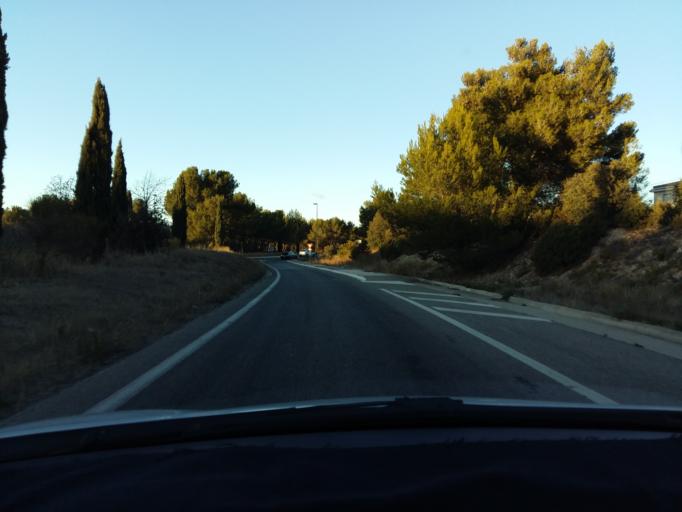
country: FR
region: Provence-Alpes-Cote d'Azur
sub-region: Departement des Bouches-du-Rhone
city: Cabries
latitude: 43.4942
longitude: 5.3508
